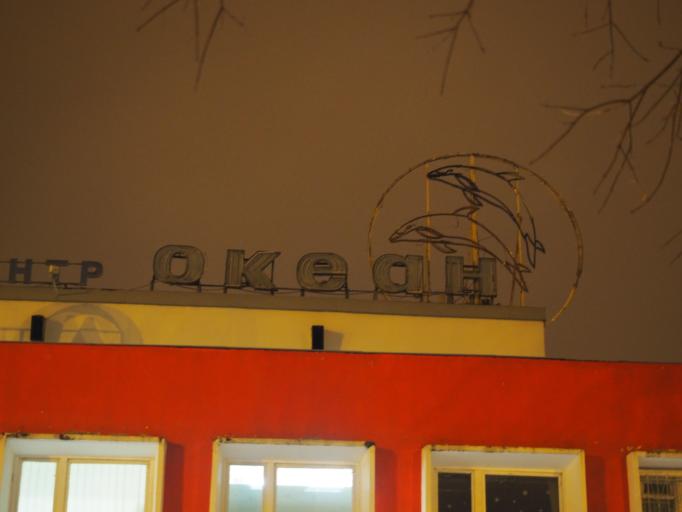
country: RU
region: Nizjnij Novgorod
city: Nizhniy Novgorod
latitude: 56.2821
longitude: 43.9235
